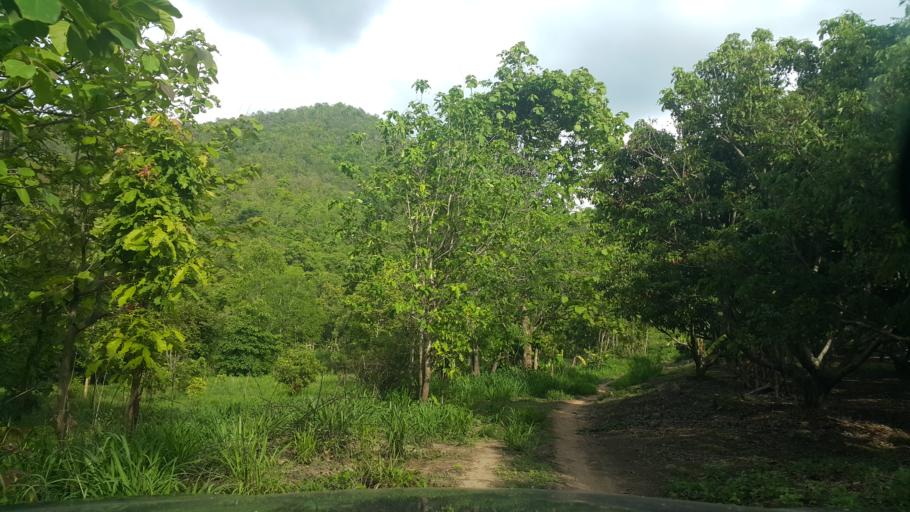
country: TH
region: Chiang Mai
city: Mae On
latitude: 18.7084
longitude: 99.2160
